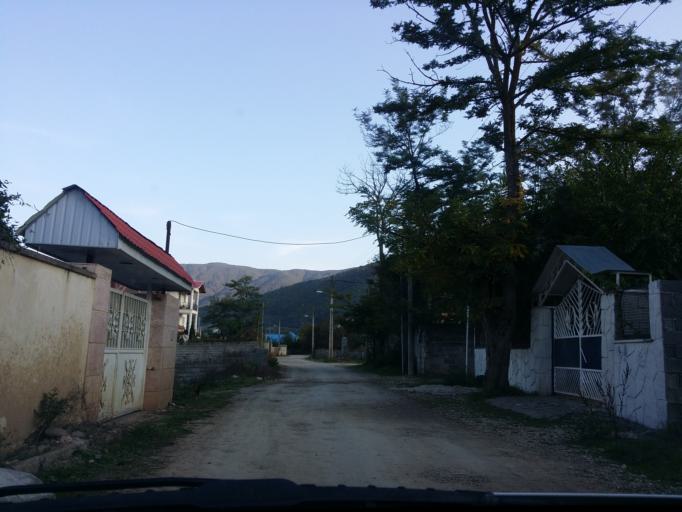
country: IR
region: Mazandaran
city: `Abbasabad
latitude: 36.5112
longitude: 51.1838
